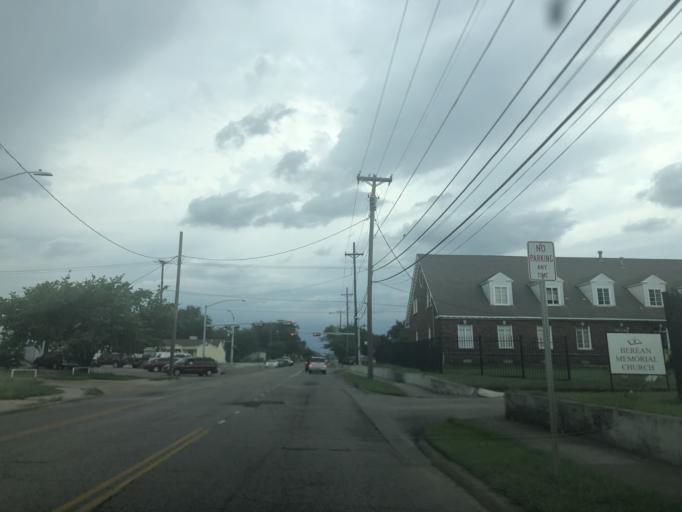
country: US
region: Texas
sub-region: Dallas County
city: Irving
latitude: 32.8077
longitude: -96.9345
